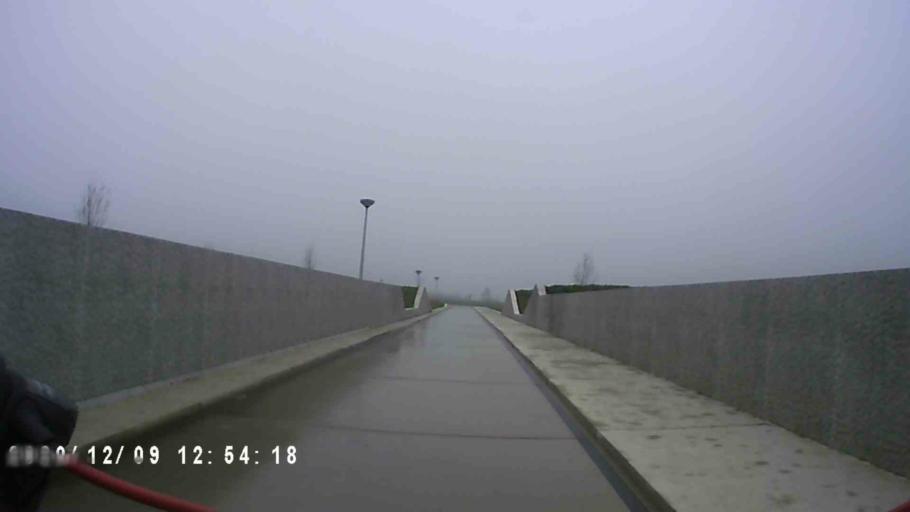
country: NL
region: Groningen
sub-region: Gemeente Groningen
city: Oosterpark
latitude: 53.2303
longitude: 6.6511
